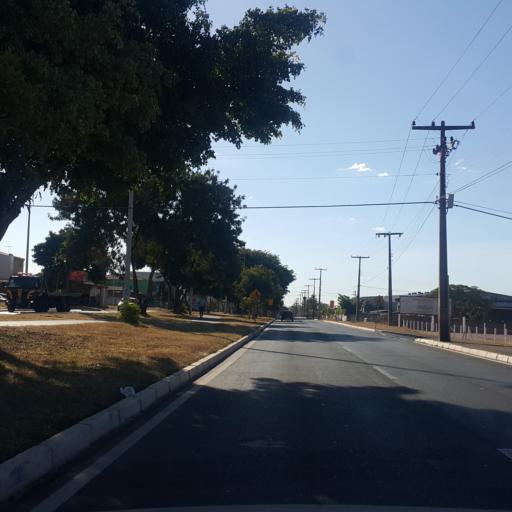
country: BR
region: Federal District
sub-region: Brasilia
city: Brasilia
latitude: -15.8113
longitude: -48.0996
